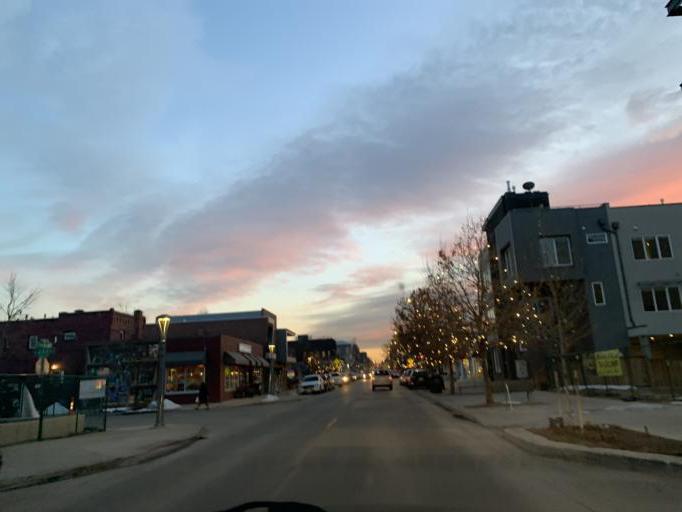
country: US
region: Colorado
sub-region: Jefferson County
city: Edgewater
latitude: 39.7756
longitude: -105.0440
